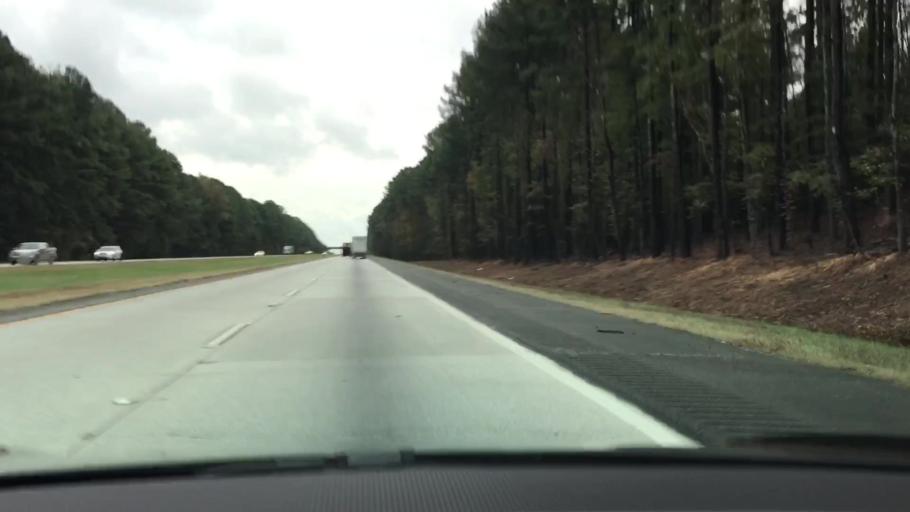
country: US
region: Georgia
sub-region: Taliaferro County
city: Crawfordville
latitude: 33.5151
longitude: -82.8553
